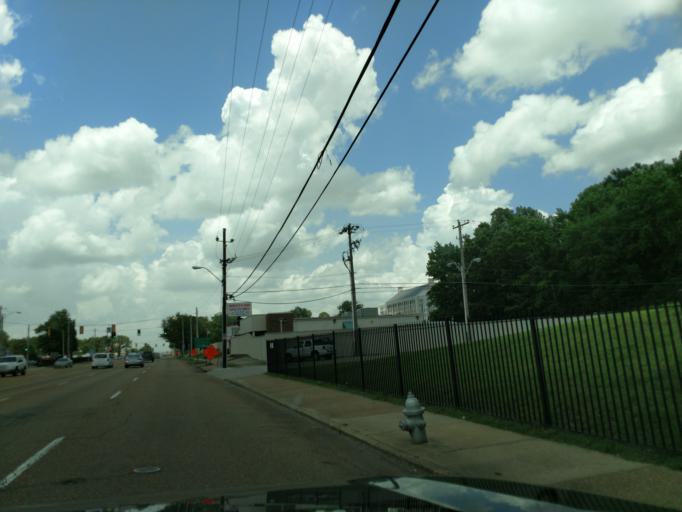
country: US
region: Tennessee
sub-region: Shelby County
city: New South Memphis
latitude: 35.0467
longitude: -90.0250
